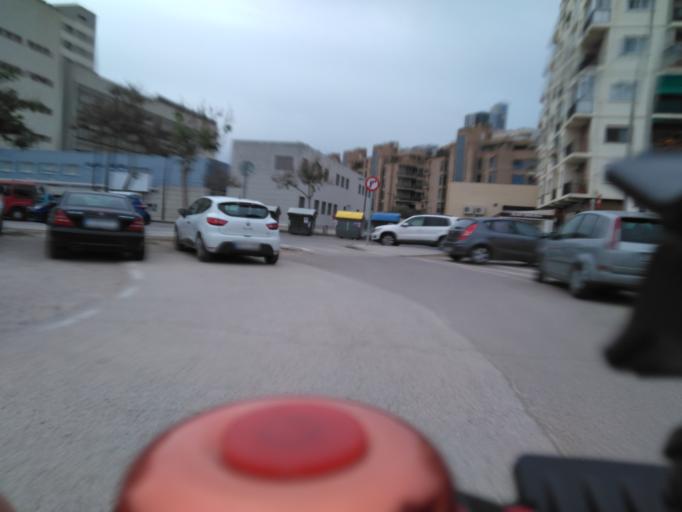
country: ES
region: Valencia
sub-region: Provincia de Valencia
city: Mislata
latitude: 39.4898
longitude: -0.4027
